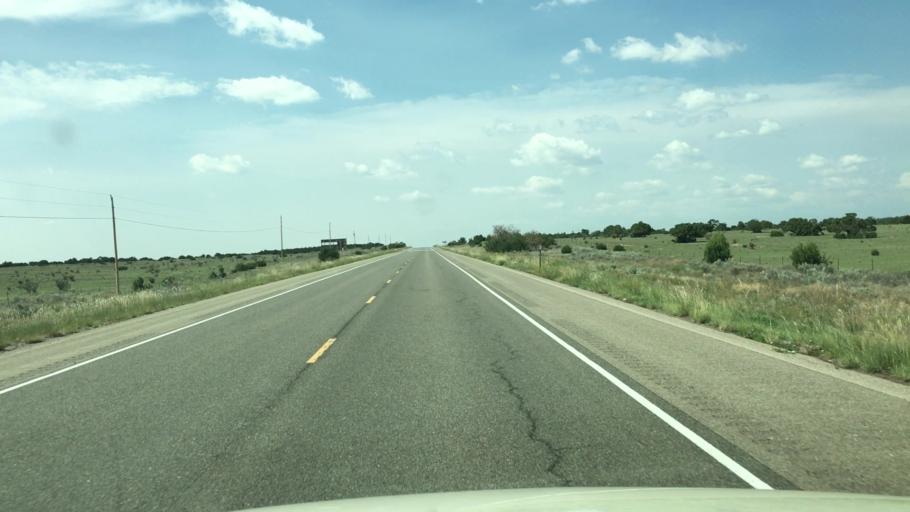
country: US
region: New Mexico
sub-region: Torrance County
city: Moriarty
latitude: 35.0383
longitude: -105.6810
